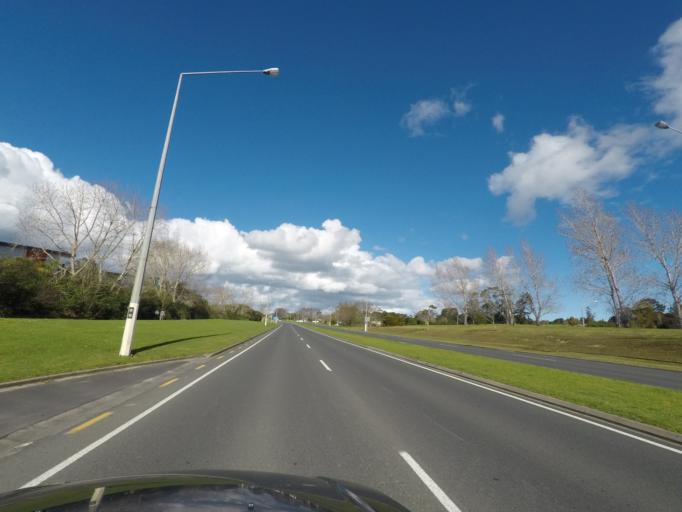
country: NZ
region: Auckland
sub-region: Auckland
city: Rothesay Bay
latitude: -36.7317
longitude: 174.7048
